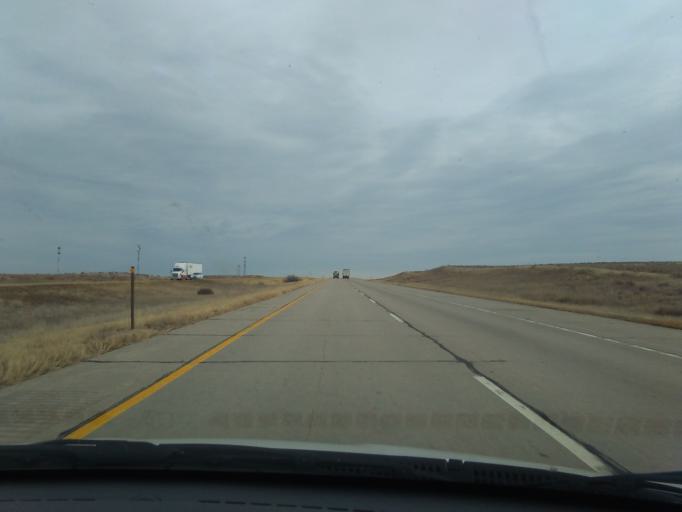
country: US
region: Colorado
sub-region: Weld County
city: Keenesburg
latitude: 40.2215
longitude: -104.1984
